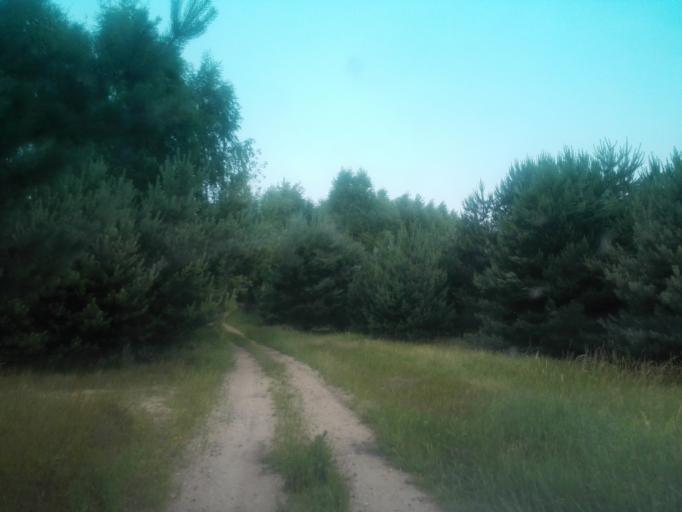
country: PL
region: Silesian Voivodeship
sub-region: Powiat czestochowski
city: Olsztyn
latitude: 50.7907
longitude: 19.2554
